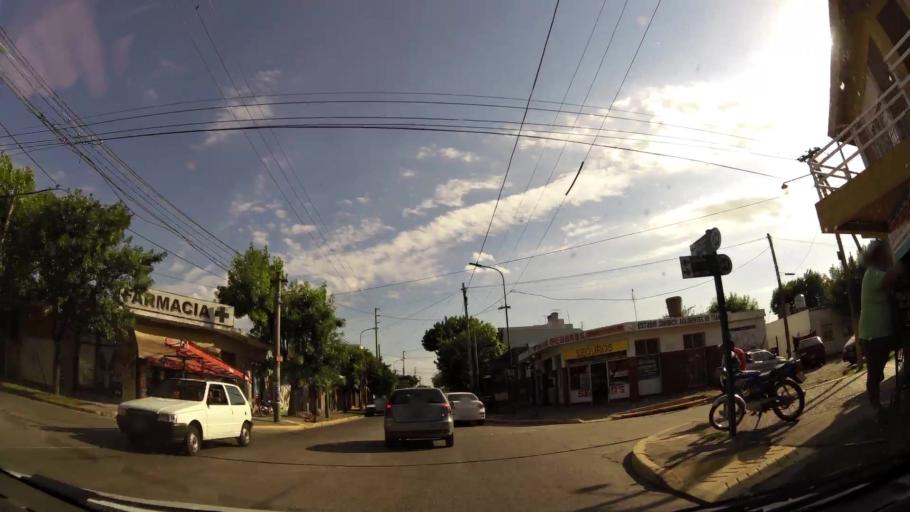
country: AR
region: Buenos Aires
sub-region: Partido de Merlo
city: Merlo
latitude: -34.6575
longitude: -58.7245
